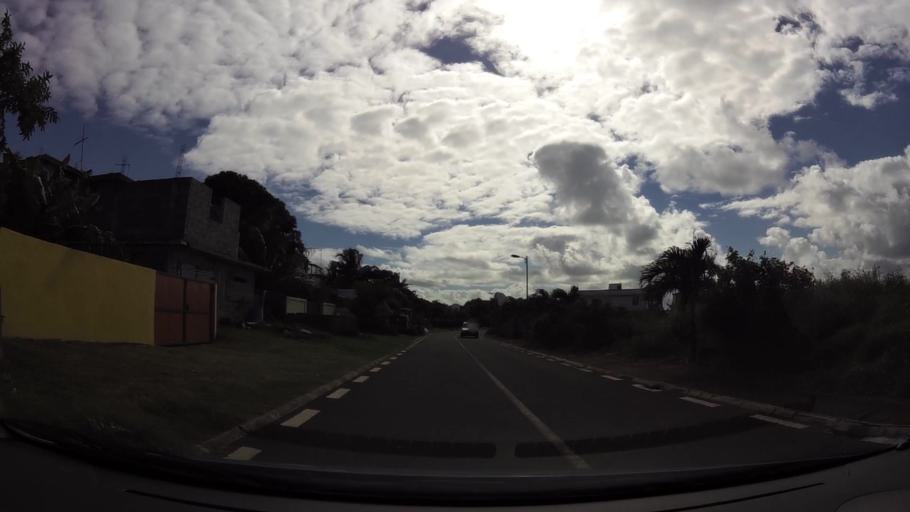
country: MU
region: Grand Port
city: Beau Vallon
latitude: -20.4226
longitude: 57.7061
